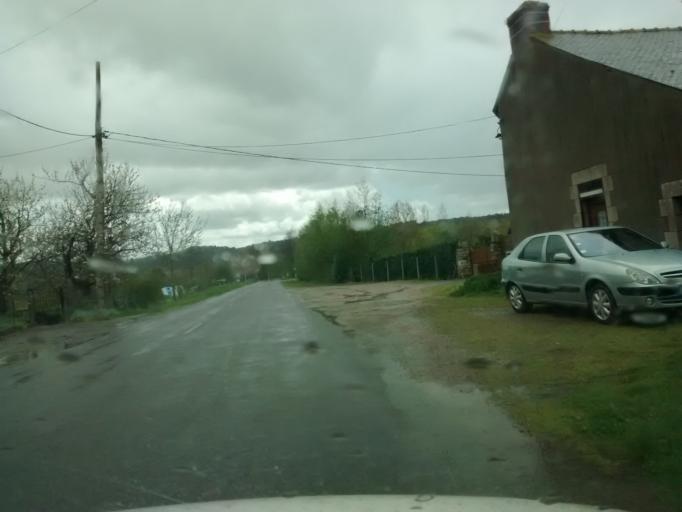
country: FR
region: Brittany
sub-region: Departement du Morbihan
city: Pleucadeuc
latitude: 47.7607
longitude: -2.3172
